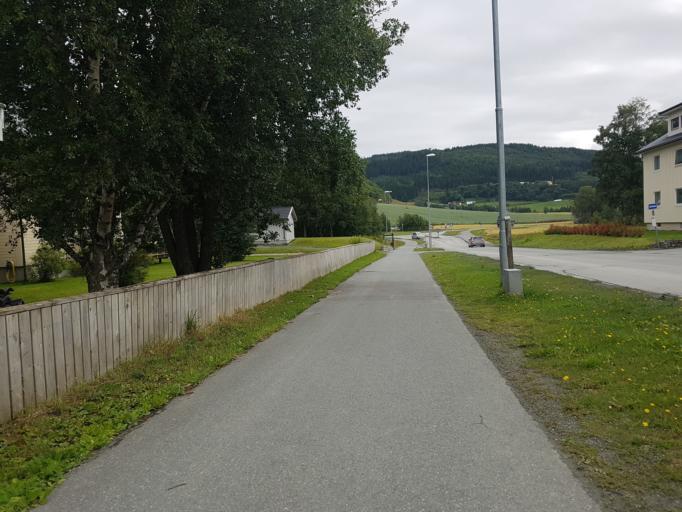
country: NO
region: Sor-Trondelag
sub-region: Trondheim
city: Trondheim
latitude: 63.3836
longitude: 10.4320
